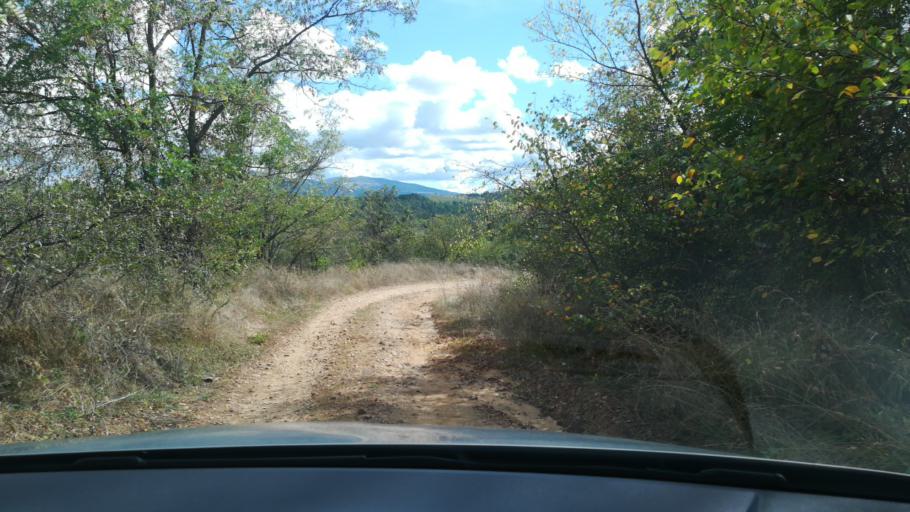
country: MK
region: Delcevo
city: Delcevo
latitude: 41.8895
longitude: 22.8052
